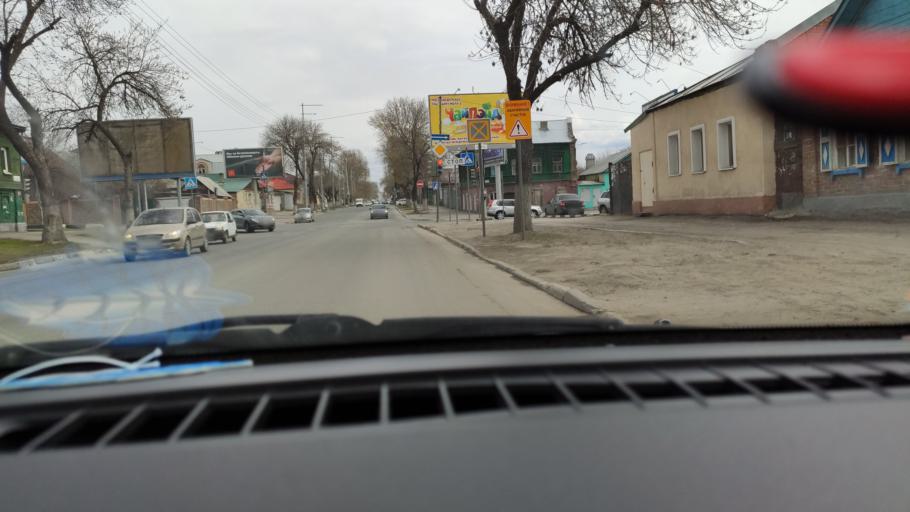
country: RU
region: Saratov
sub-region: Saratovskiy Rayon
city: Saratov
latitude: 51.5420
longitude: 46.0347
